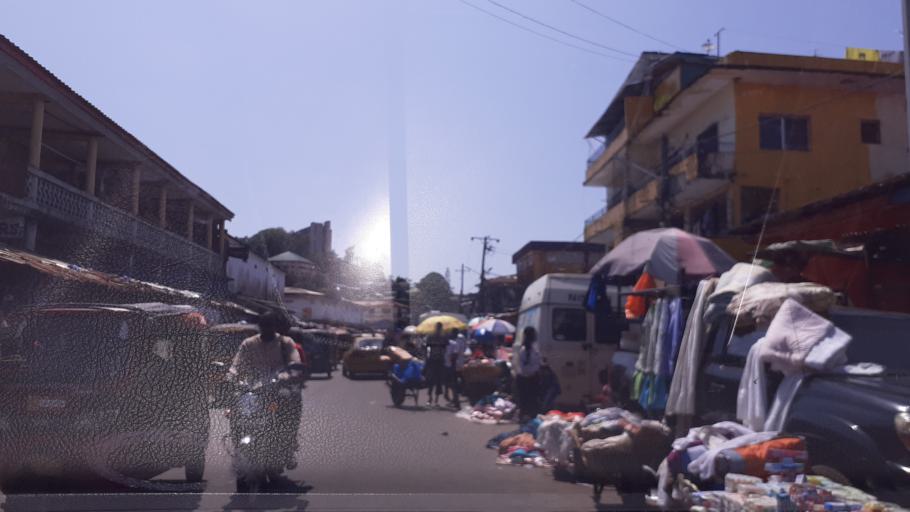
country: LR
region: Montserrado
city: Monrovia
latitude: 6.3221
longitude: -10.8069
